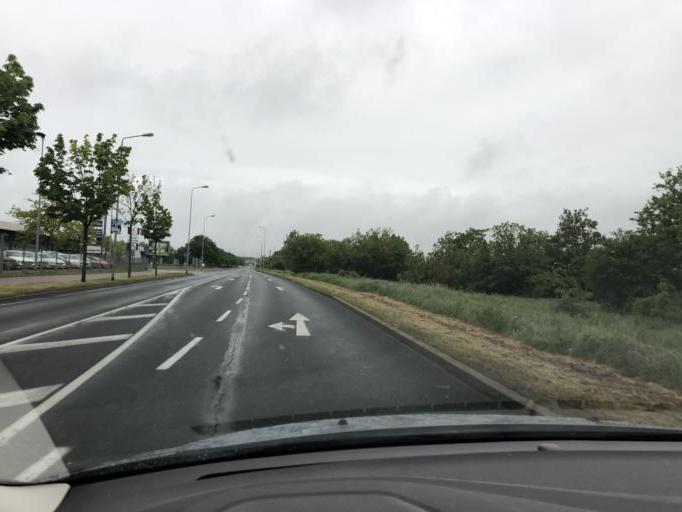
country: DE
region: Saxony-Anhalt
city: Dessau
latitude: 51.8191
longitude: 12.2156
